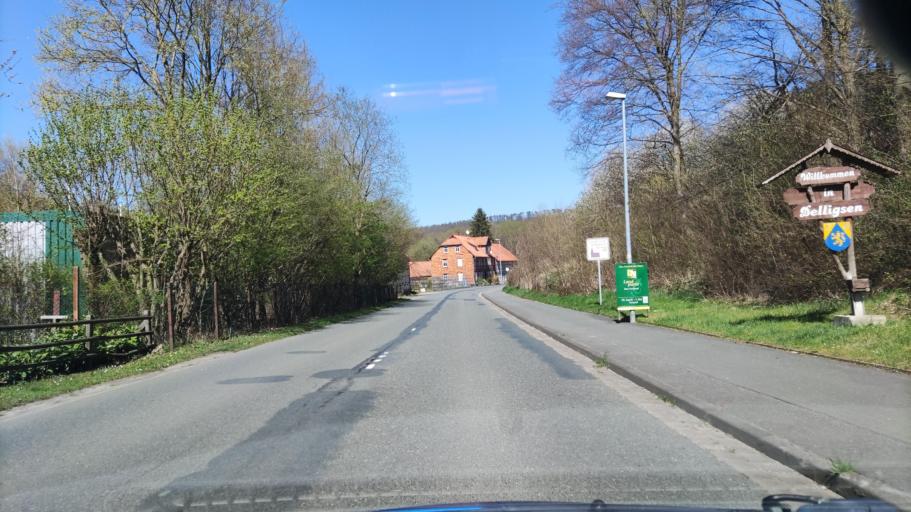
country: DE
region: Lower Saxony
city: Delligsen
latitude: 51.9377
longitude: 9.7873
